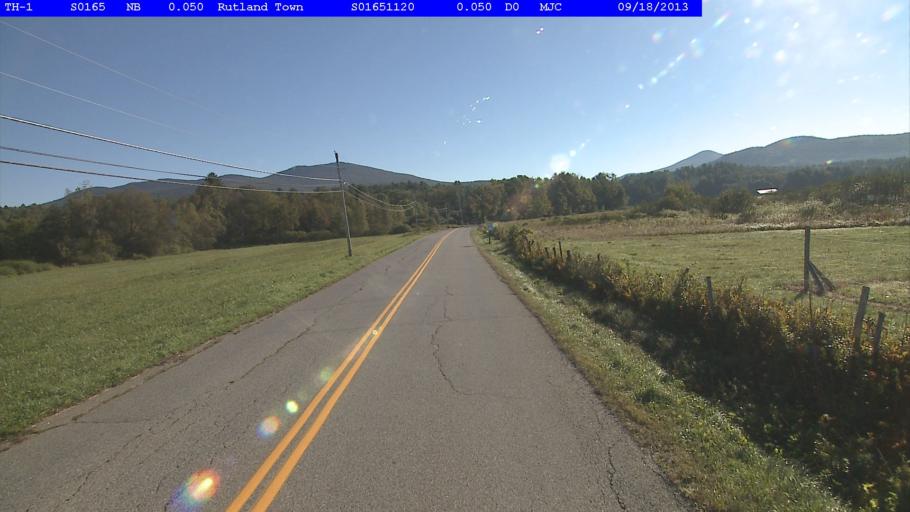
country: US
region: Vermont
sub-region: Rutland County
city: Rutland
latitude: 43.6518
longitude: -72.9712
